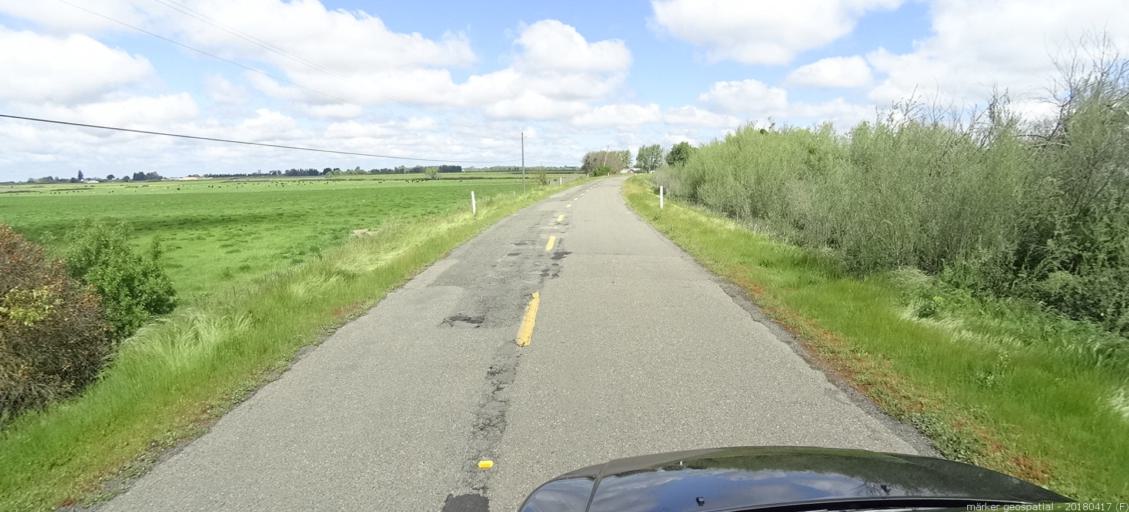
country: US
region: California
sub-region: Sacramento County
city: Walnut Grove
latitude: 38.2054
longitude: -121.5416
